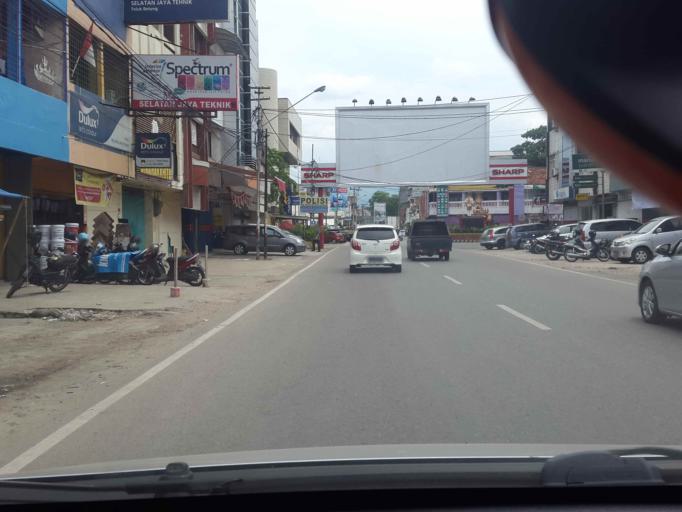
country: ID
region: Lampung
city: Bandarlampung
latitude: -5.4483
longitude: 105.2676
